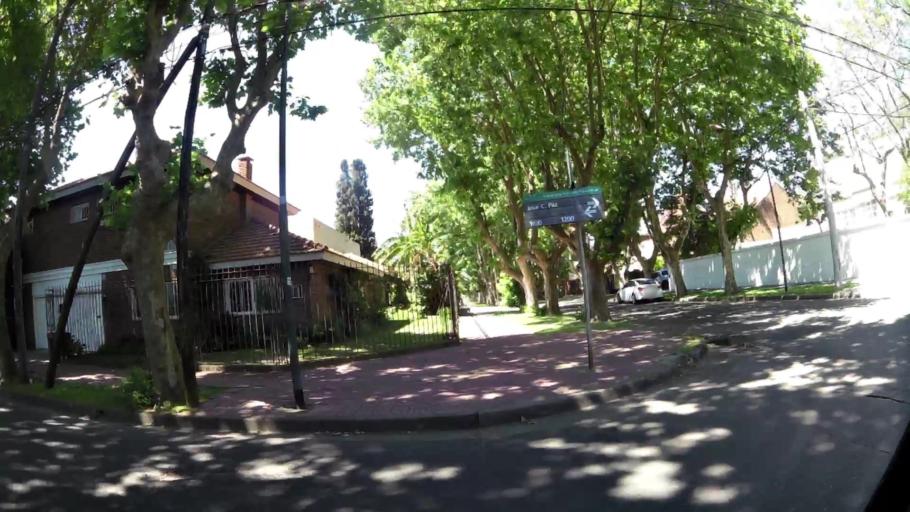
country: AR
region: Buenos Aires
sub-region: Partido de San Isidro
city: San Isidro
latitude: -34.4776
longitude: -58.4932
